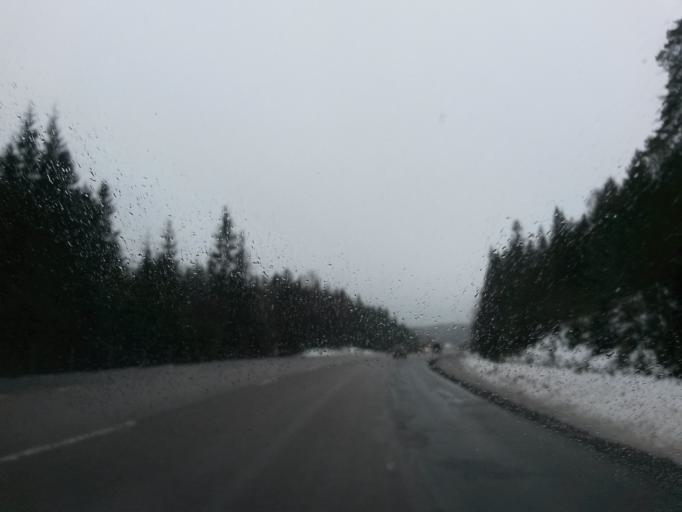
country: SE
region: Vaestra Goetaland
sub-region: Boras Kommun
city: Boras
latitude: 57.6669
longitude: 12.9197
